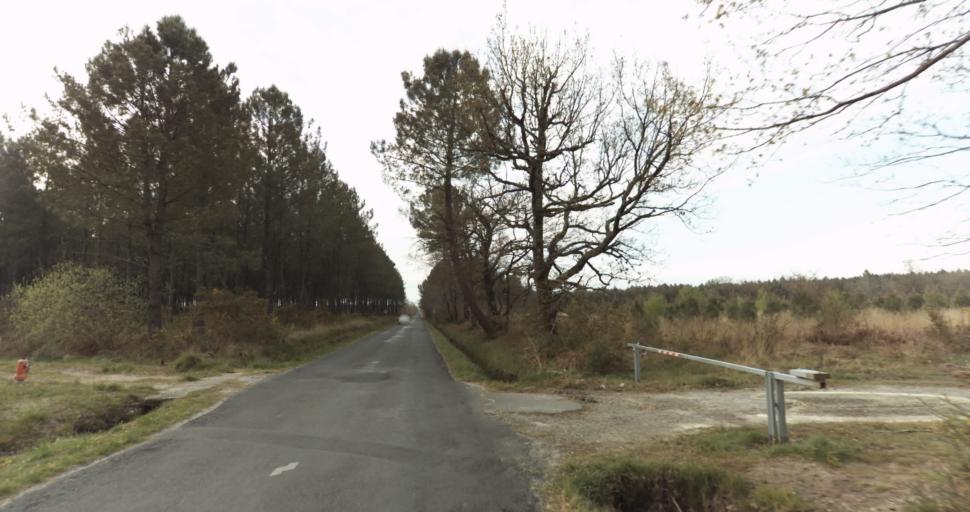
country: FR
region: Aquitaine
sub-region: Departement de la Gironde
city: Martignas-sur-Jalle
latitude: 44.8015
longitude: -0.7677
